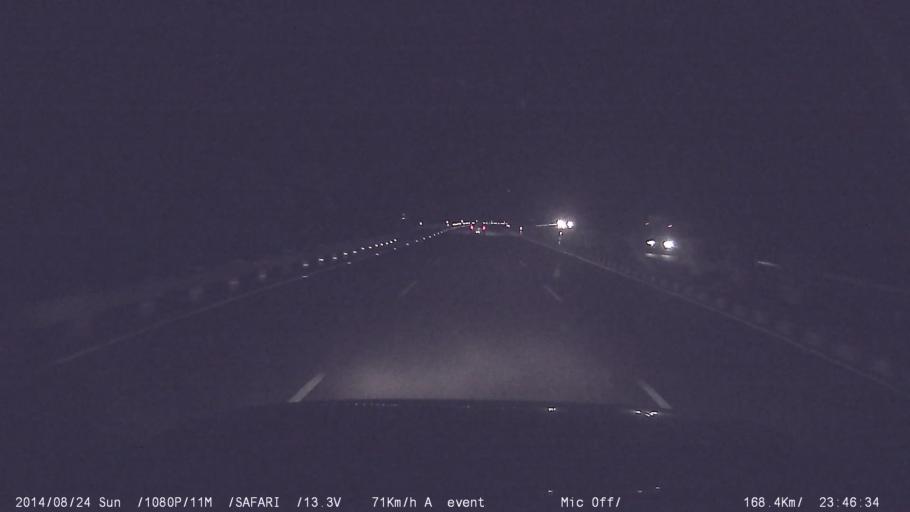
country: IN
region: Tamil Nadu
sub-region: Krishnagiri
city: Krishnagiri
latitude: 12.5522
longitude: 78.3483
